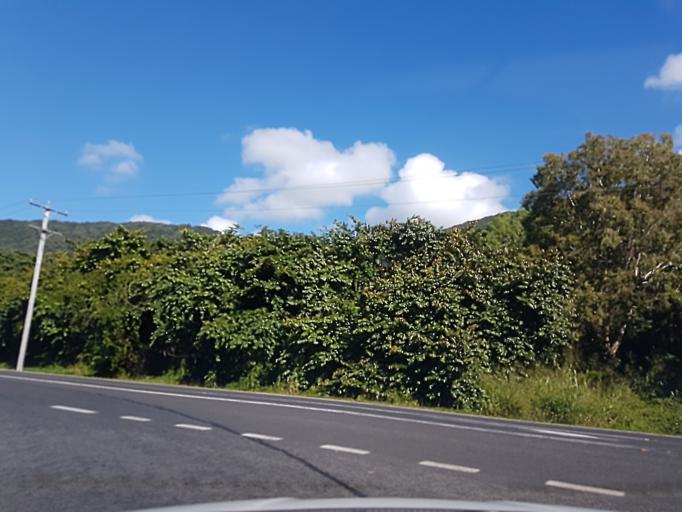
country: AU
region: Queensland
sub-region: Cairns
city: Palm Cove
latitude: -16.7454
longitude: 145.6637
